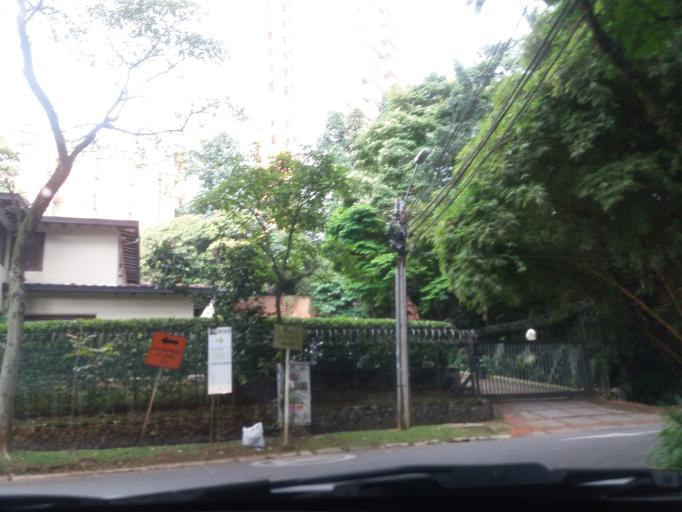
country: CO
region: Antioquia
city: Envigado
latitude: 6.1907
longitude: -75.5752
